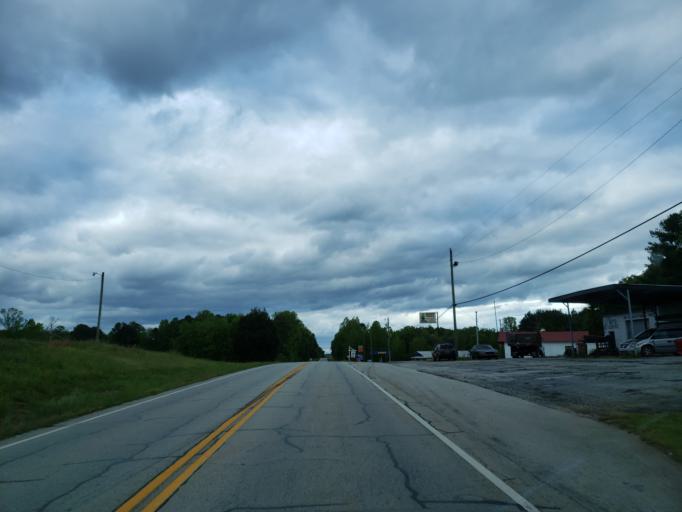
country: US
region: Georgia
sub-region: Haralson County
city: Buchanan
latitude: 33.8196
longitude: -85.0899
